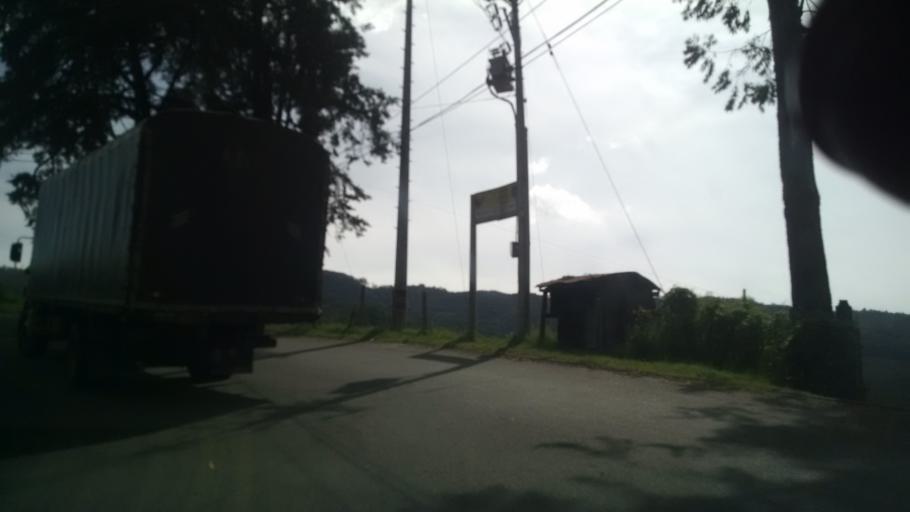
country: CO
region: Antioquia
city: Caldas
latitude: 6.0346
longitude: -75.6251
